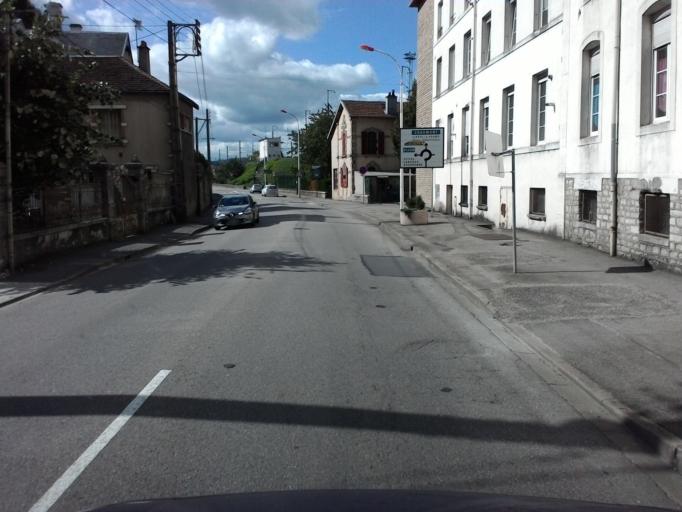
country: FR
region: Lorraine
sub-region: Departement des Vosges
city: Neufchateau
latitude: 48.3553
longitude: 5.6889
